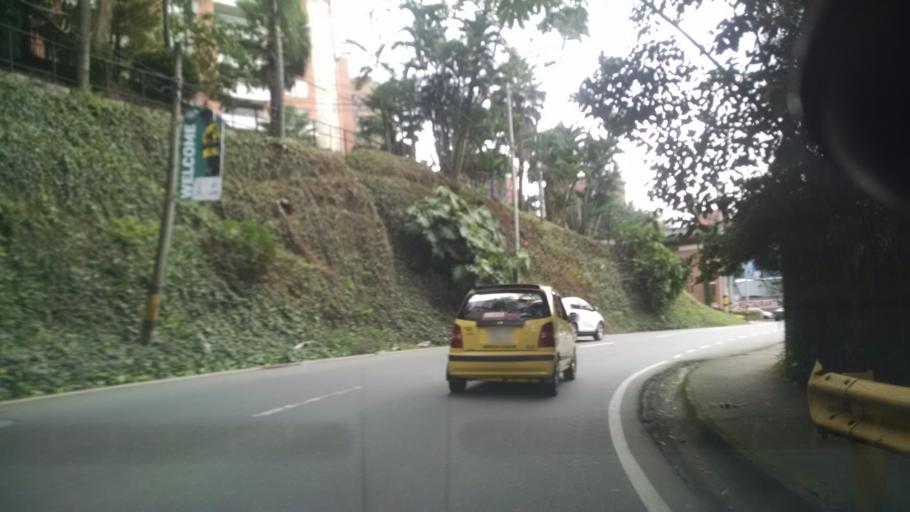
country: CO
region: Antioquia
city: Envigado
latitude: 6.2069
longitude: -75.5594
